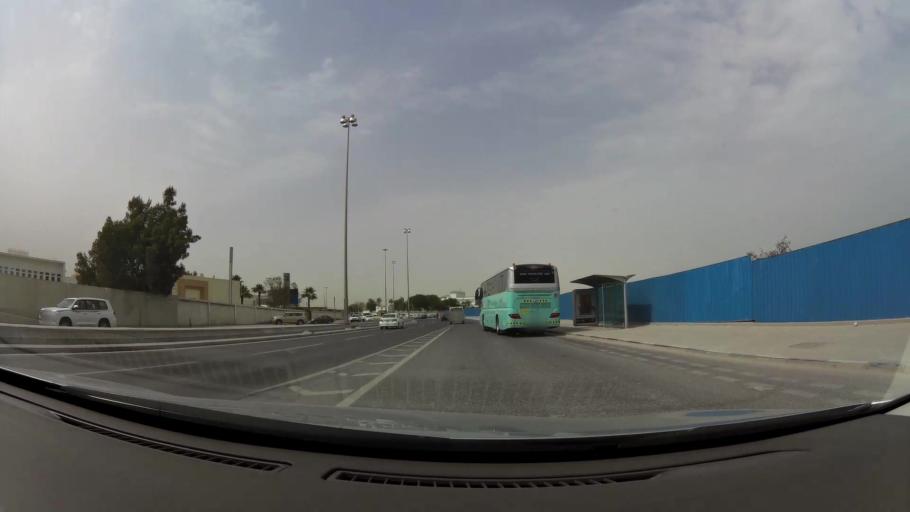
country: QA
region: Baladiyat ad Dawhah
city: Doha
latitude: 25.2924
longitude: 51.5151
